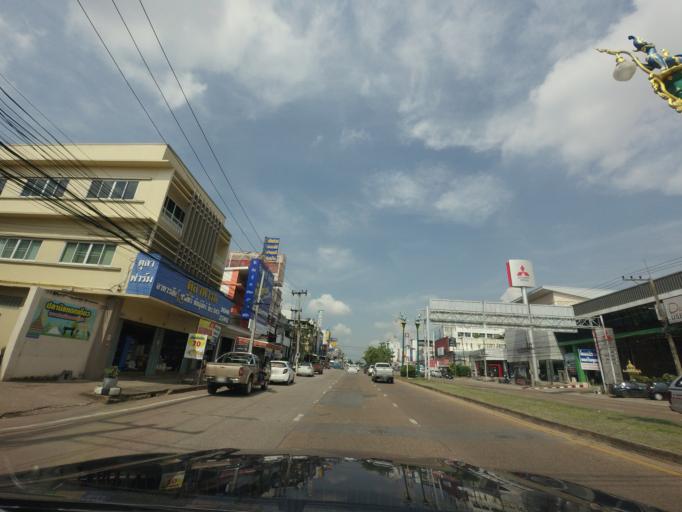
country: TH
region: Khon Kaen
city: Khon Kaen
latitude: 16.4397
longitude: 102.8273
